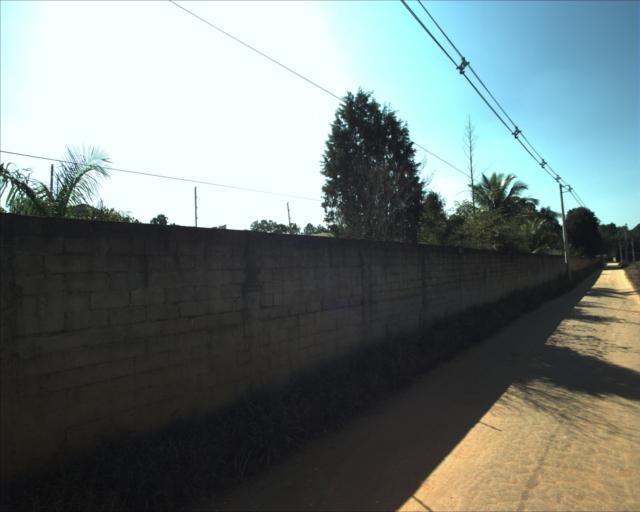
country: BR
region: Sao Paulo
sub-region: Aracoiaba Da Serra
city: Aracoiaba da Serra
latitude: -23.4835
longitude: -47.5392
